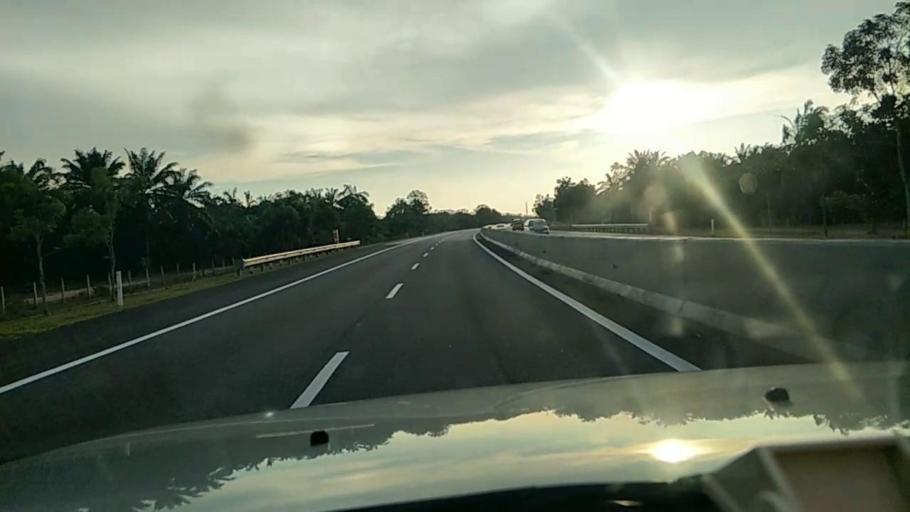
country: MY
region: Selangor
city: Batu Arang
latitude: 3.2877
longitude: 101.4205
